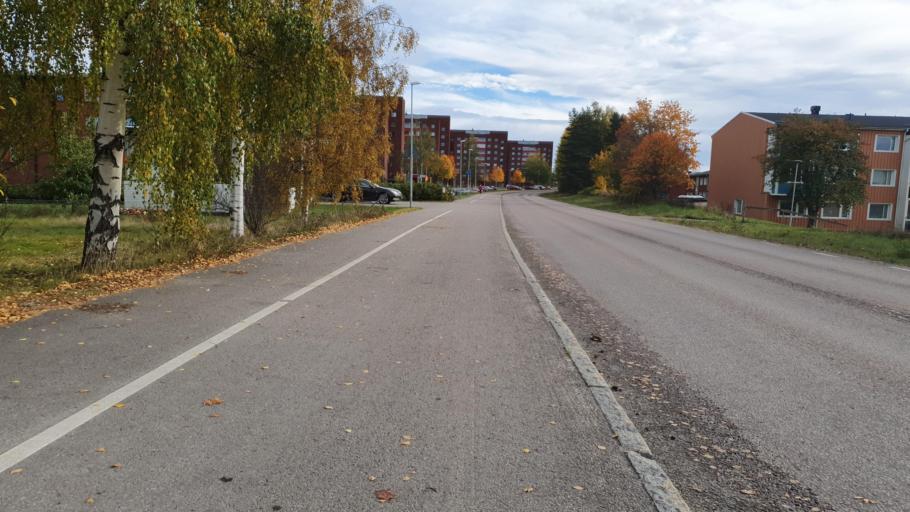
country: SE
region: Vaesternorrland
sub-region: Sundsvalls Kommun
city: Sundsvall
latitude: 62.4050
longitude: 17.2460
